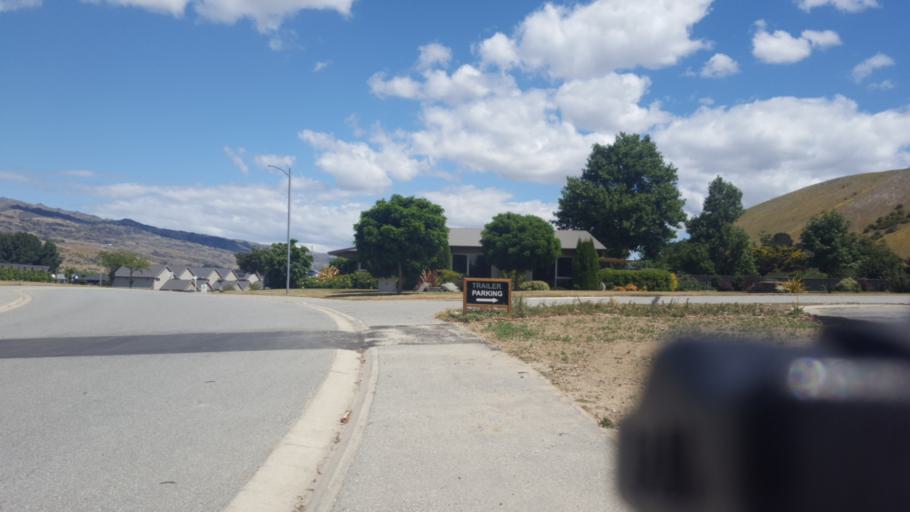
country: NZ
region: Otago
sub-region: Queenstown-Lakes District
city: Wanaka
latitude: -44.9781
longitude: 169.2360
